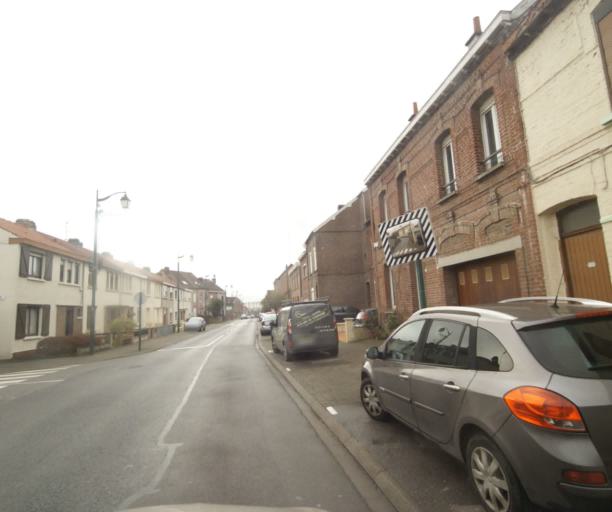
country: FR
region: Nord-Pas-de-Calais
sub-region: Departement du Nord
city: Aulnoy-lez-Valenciennes
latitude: 50.3360
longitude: 3.5275
